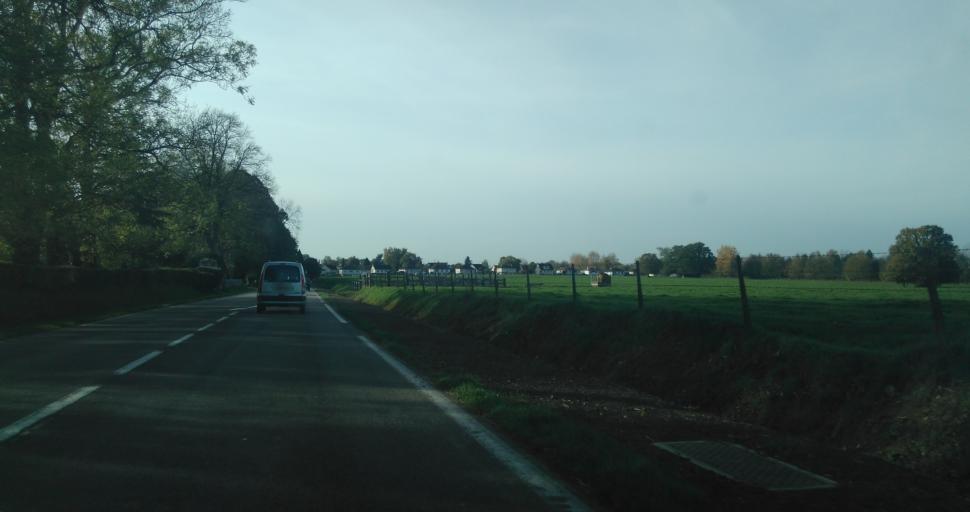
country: FR
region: Haute-Normandie
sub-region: Departement de l'Eure
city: Saint-Ouen-de-Thouberville
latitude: 49.3595
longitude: 0.8580
